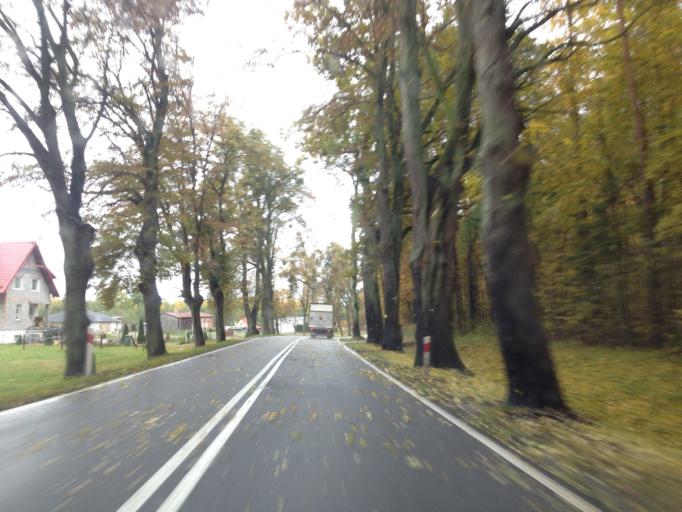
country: PL
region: Pomeranian Voivodeship
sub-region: Powiat kwidzynski
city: Ryjewo
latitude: 53.8610
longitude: 19.0015
